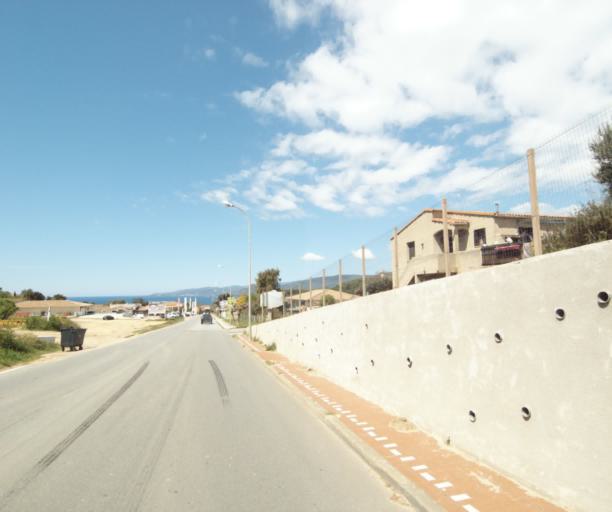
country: FR
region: Corsica
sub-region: Departement de la Corse-du-Sud
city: Propriano
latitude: 41.6698
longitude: 8.9156
